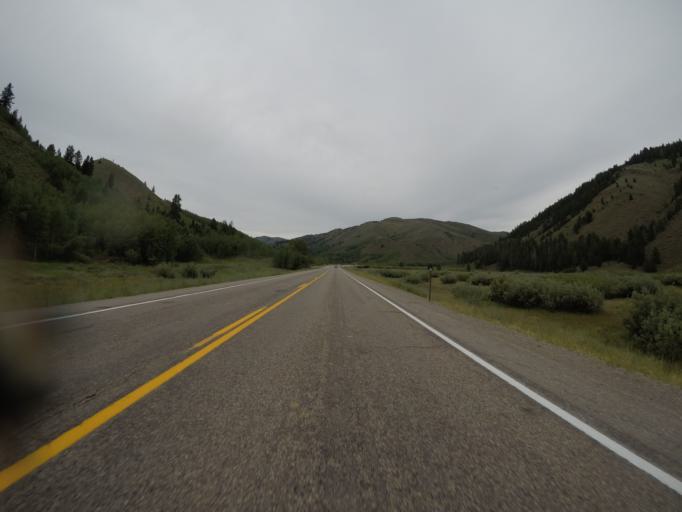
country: US
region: Wyoming
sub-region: Lincoln County
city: Afton
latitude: 42.4808
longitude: -110.9633
